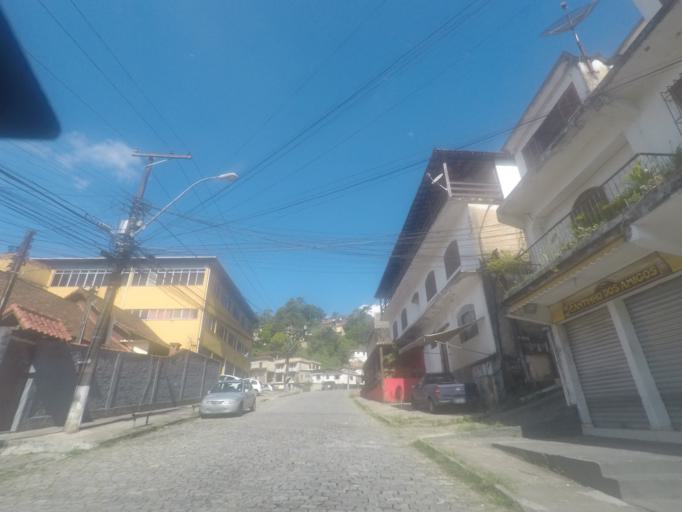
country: BR
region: Rio de Janeiro
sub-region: Petropolis
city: Petropolis
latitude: -22.5216
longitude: -43.2008
